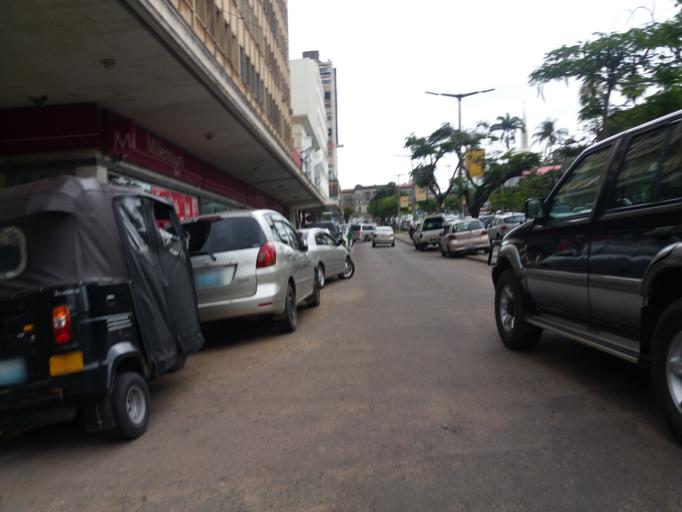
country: MZ
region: Maputo City
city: Maputo
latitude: -25.9716
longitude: 32.5716
